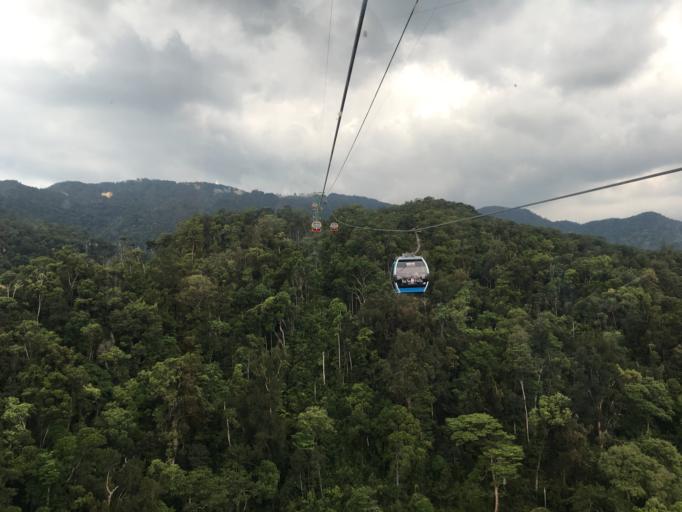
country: VN
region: Da Nang
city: Hoa Vang
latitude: 16.0141
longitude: 108.0123
